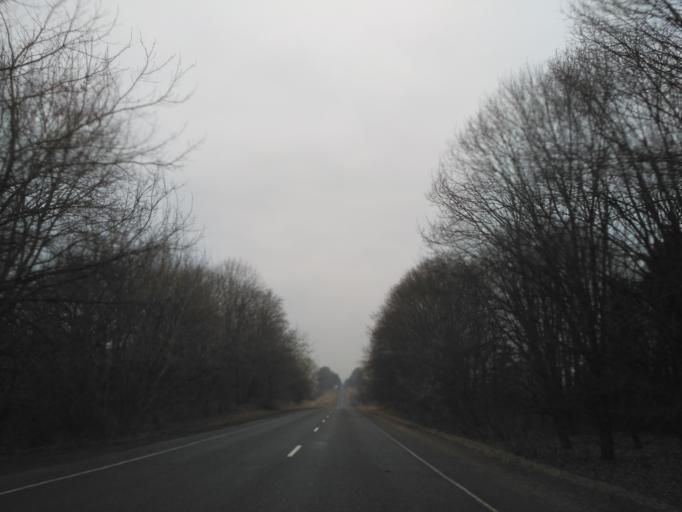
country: BY
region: Minsk
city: Snow
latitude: 53.2549
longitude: 26.2925
